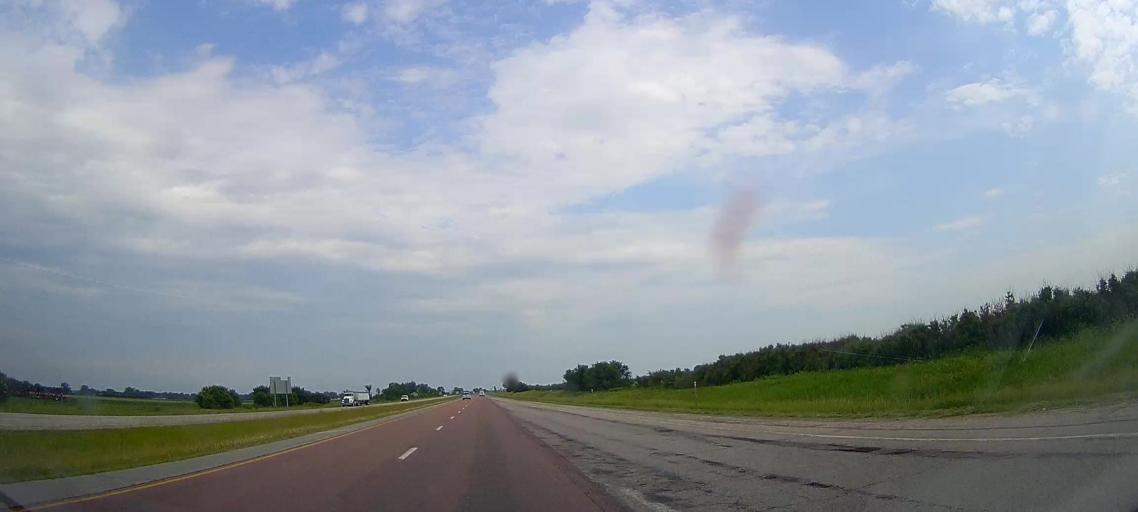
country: US
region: Iowa
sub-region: Monona County
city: Onawa
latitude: 42.0225
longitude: -96.1291
